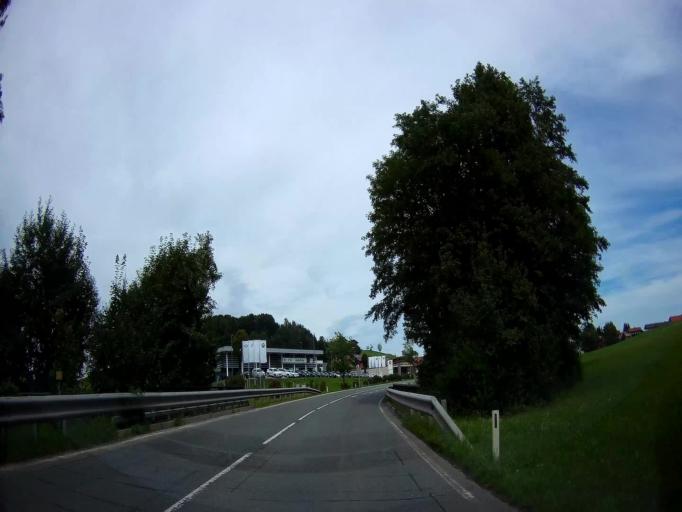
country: AT
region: Salzburg
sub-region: Politischer Bezirk Salzburg-Umgebung
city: Eugendorf
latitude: 47.8531
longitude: 13.1080
